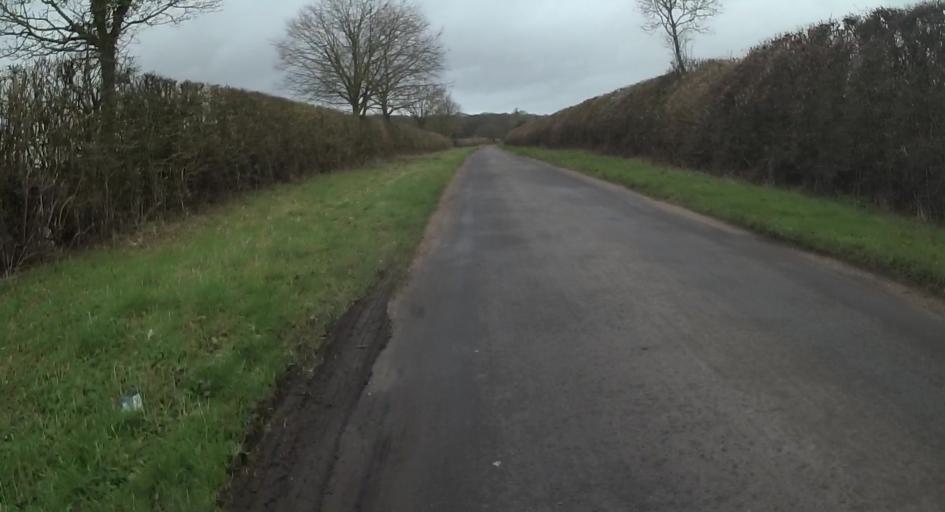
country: GB
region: England
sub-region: Hampshire
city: Overton
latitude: 51.2706
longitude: -1.1991
